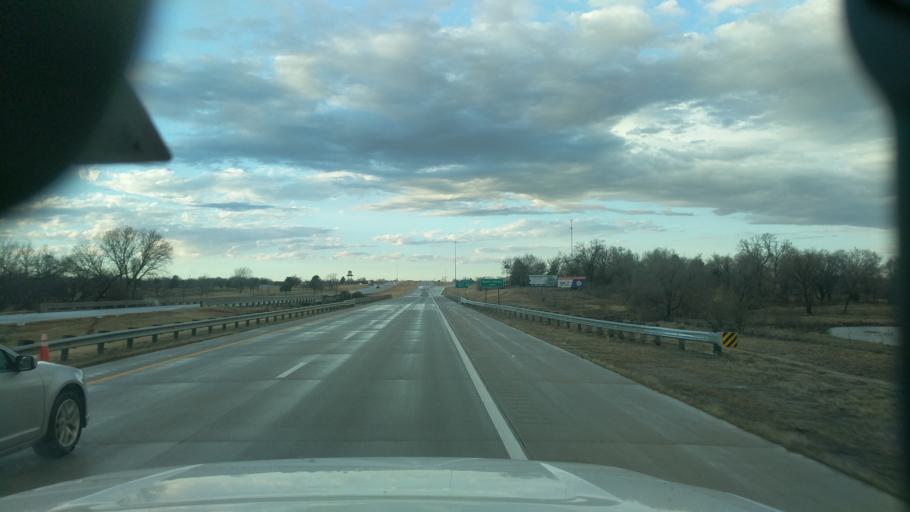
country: US
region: Kansas
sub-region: Harvey County
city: Hesston
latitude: 38.1399
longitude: -97.4113
